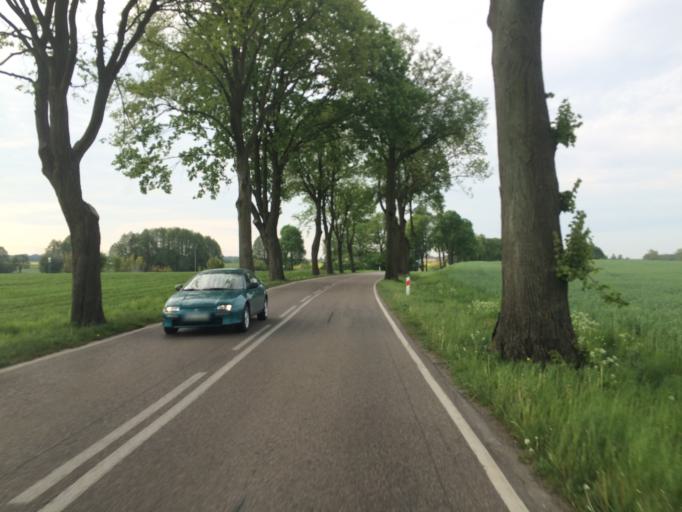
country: PL
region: Warmian-Masurian Voivodeship
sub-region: Powiat dzialdowski
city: Dzialdowo
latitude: 53.2821
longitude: 20.1435
